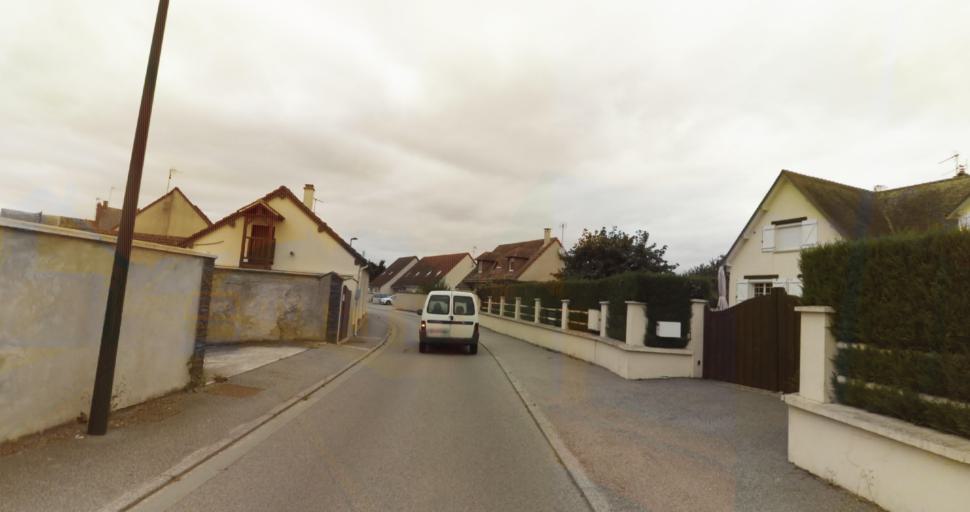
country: FR
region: Haute-Normandie
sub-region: Departement de l'Eure
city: Marcilly-sur-Eure
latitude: 48.9092
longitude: 1.2766
